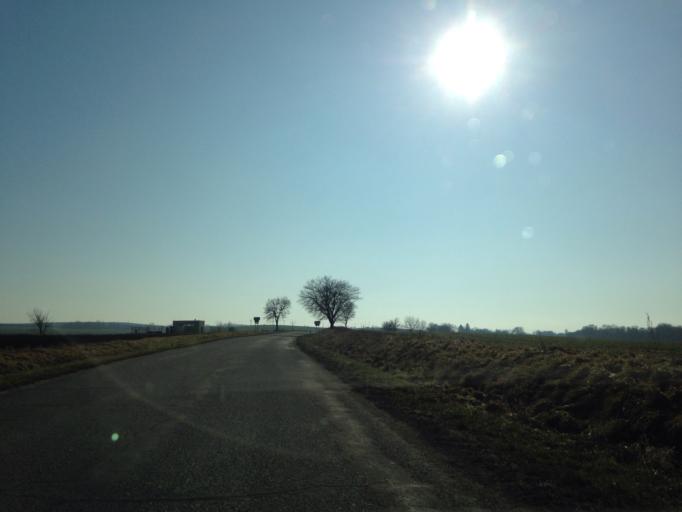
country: SK
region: Nitriansky
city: Svodin
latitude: 47.9177
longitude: 18.4057
